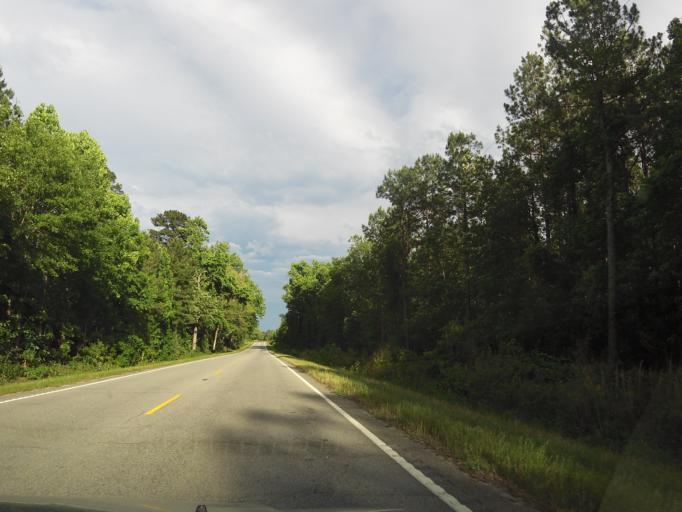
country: US
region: South Carolina
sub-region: Hampton County
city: Estill
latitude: 32.6026
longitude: -81.2340
